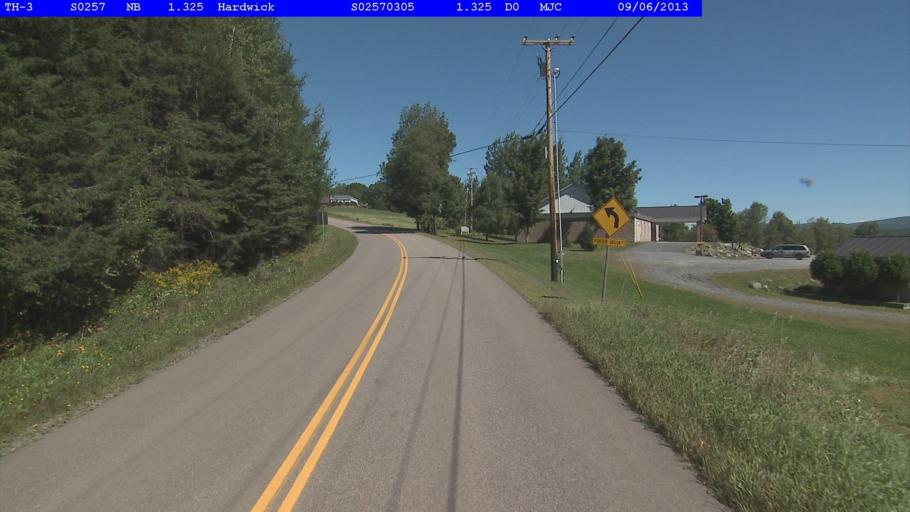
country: US
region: Vermont
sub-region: Caledonia County
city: Hardwick
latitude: 44.5104
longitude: -72.3437
